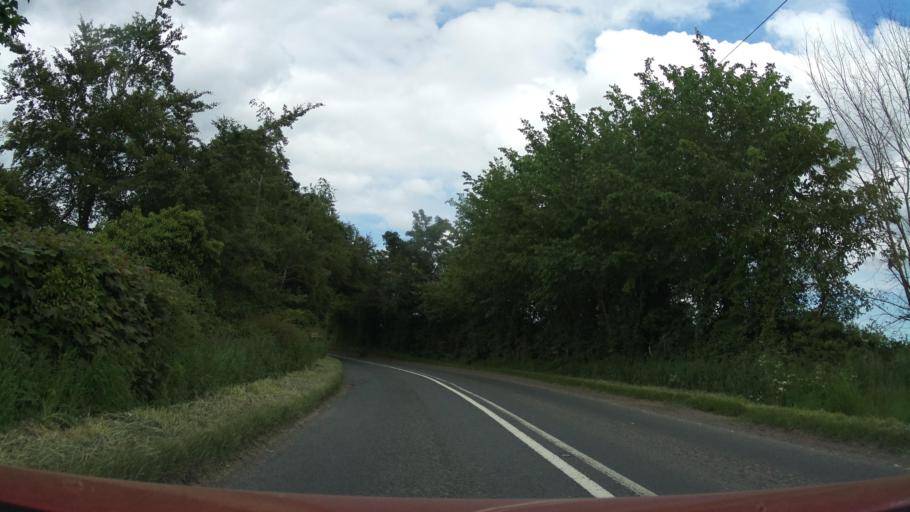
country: GB
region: England
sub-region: Herefordshire
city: Ross on Wye
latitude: 51.9427
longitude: -2.5527
